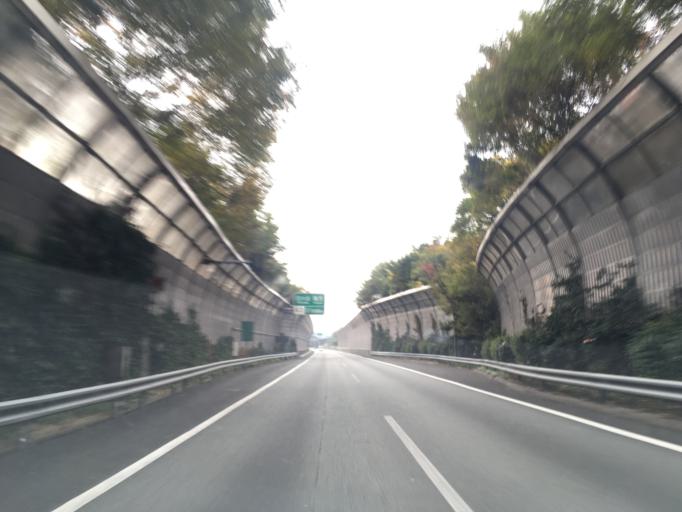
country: JP
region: Tokyo
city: Fussa
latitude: 35.7436
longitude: 139.2820
